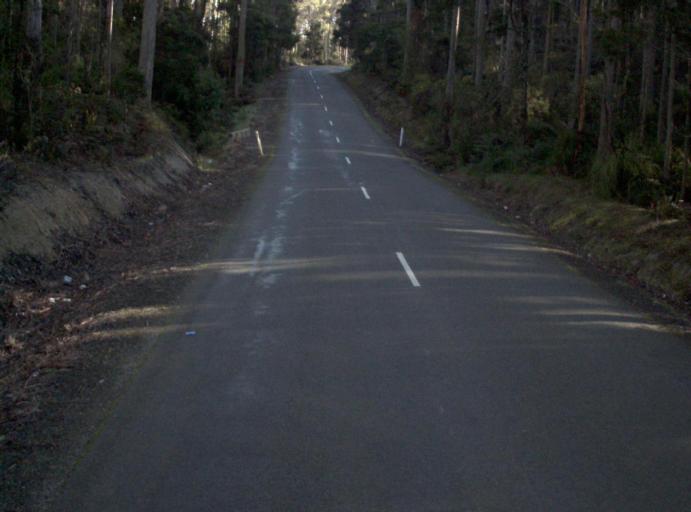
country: AU
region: Tasmania
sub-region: Dorset
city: Bridport
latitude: -41.1588
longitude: 147.2386
